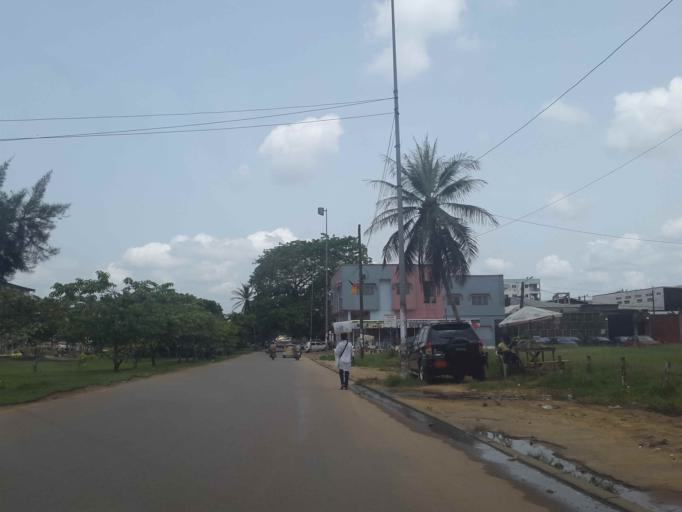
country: CM
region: Littoral
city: Douala
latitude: 4.0927
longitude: 9.7425
